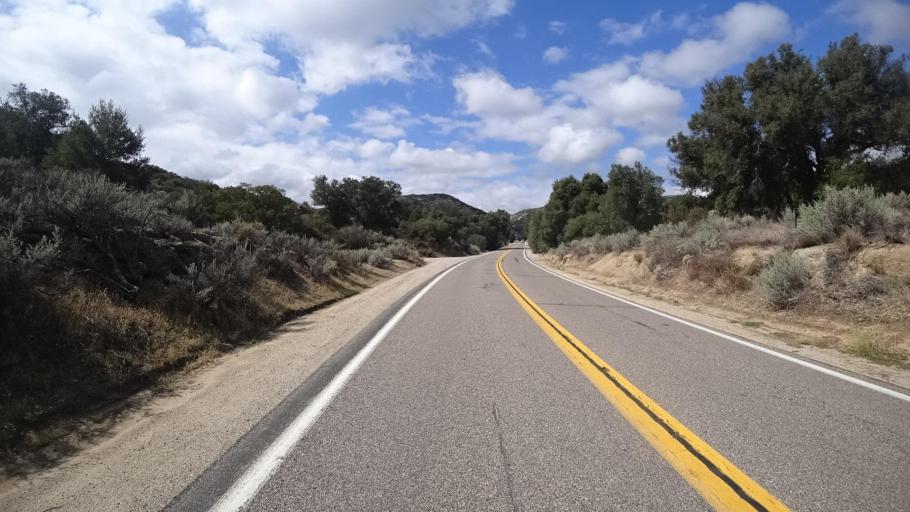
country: US
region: California
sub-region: San Diego County
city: Campo
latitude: 32.7132
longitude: -116.4959
